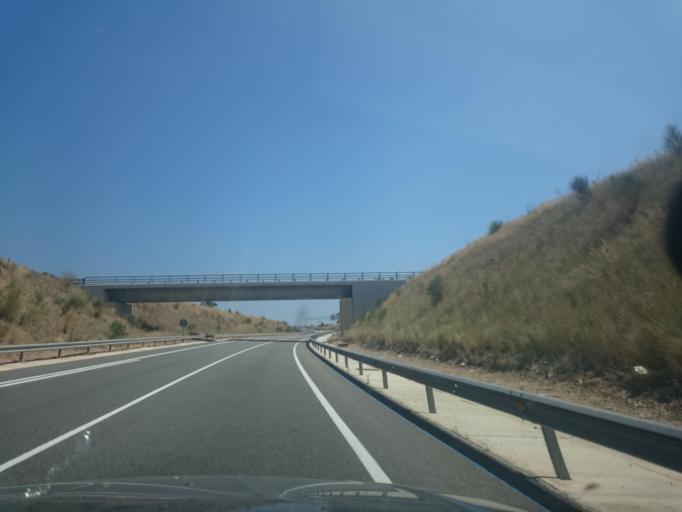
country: ES
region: Catalonia
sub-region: Provincia de Barcelona
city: Vilafranca del Penedes
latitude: 41.3453
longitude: 1.7196
